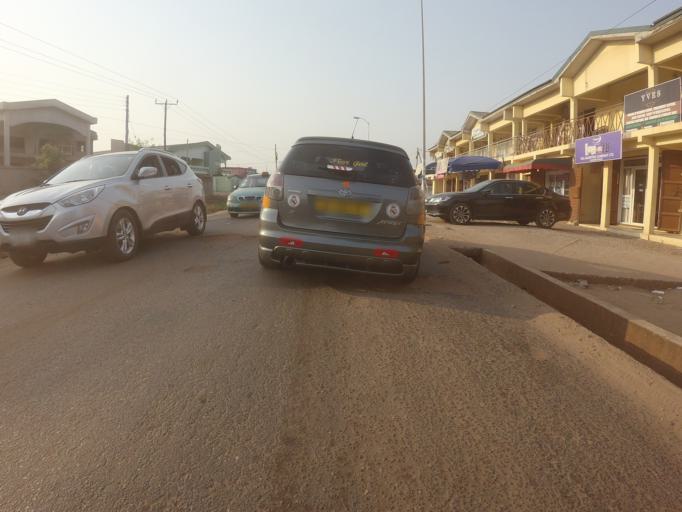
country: GH
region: Greater Accra
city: Nungua
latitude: 5.6177
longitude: -0.0531
